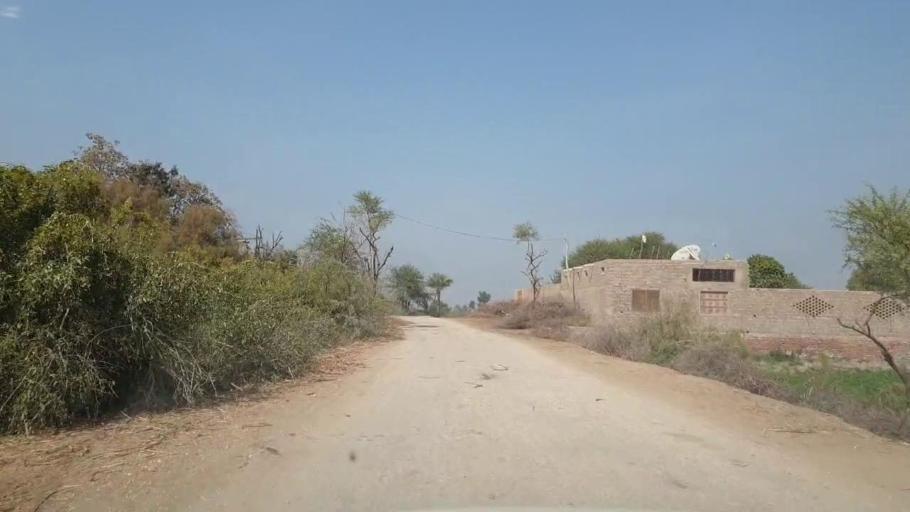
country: PK
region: Sindh
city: Mirpur Khas
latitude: 25.6869
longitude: 69.1552
